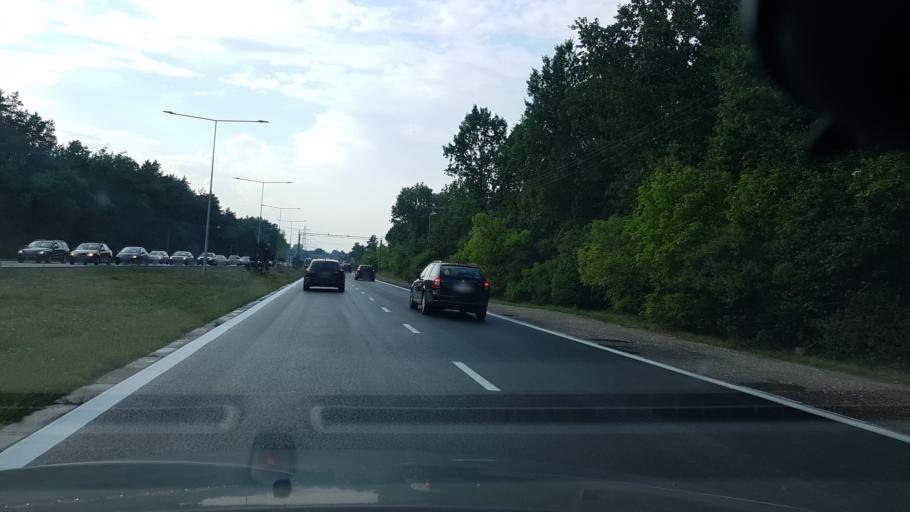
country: PL
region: Masovian Voivodeship
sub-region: Powiat warszawski zachodni
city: Lomianki
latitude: 52.3197
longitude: 20.9153
